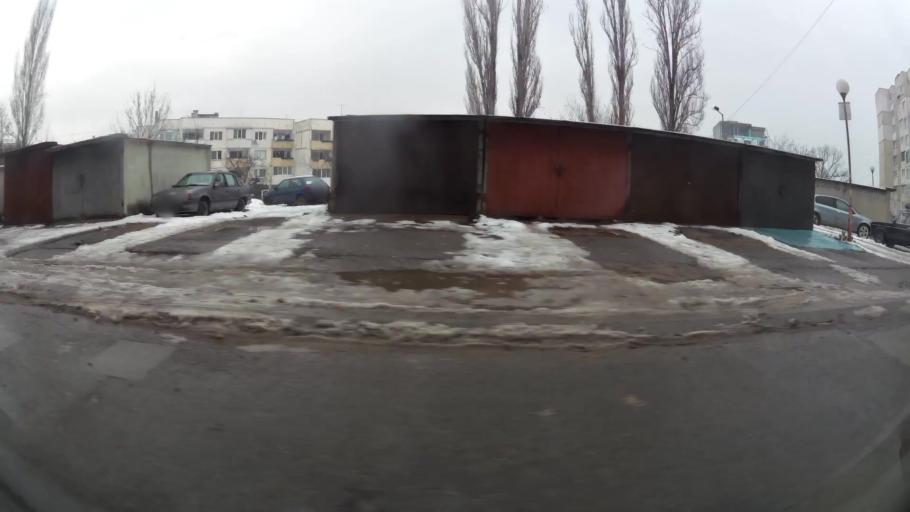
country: BG
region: Sofia-Capital
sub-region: Stolichna Obshtina
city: Sofia
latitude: 42.6847
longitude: 23.2531
